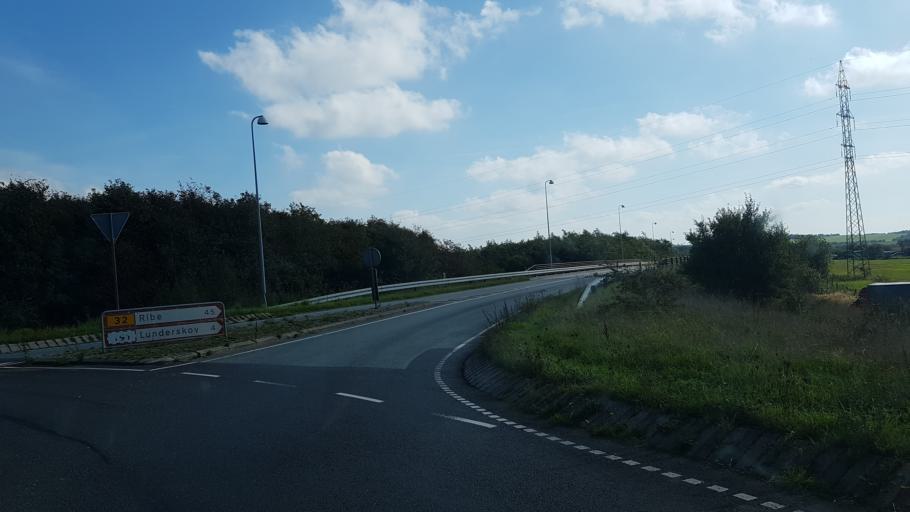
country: DK
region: South Denmark
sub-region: Kolding Kommune
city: Lunderskov
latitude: 55.5079
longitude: 9.3233
